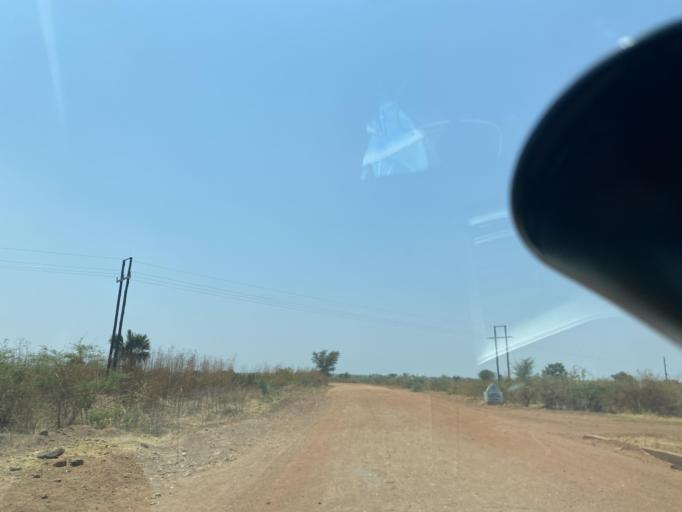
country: ZM
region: Lusaka
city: Lusaka
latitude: -15.4600
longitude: 27.9182
